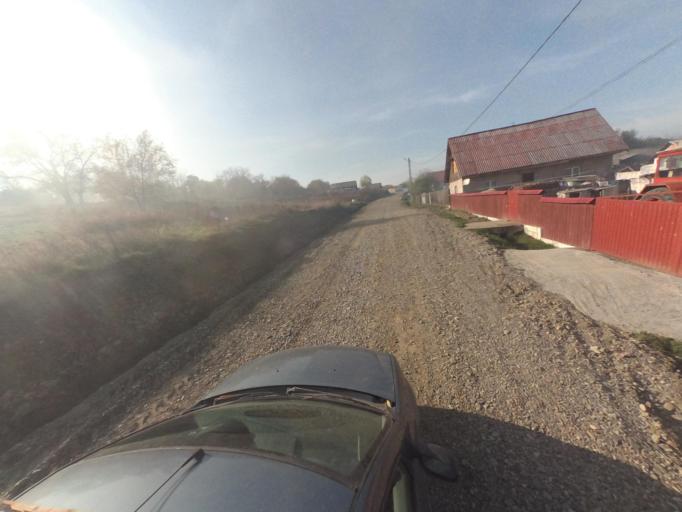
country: RO
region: Vaslui
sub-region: Comuna Bacesti
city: Bacesti
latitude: 46.8711
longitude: 27.2037
